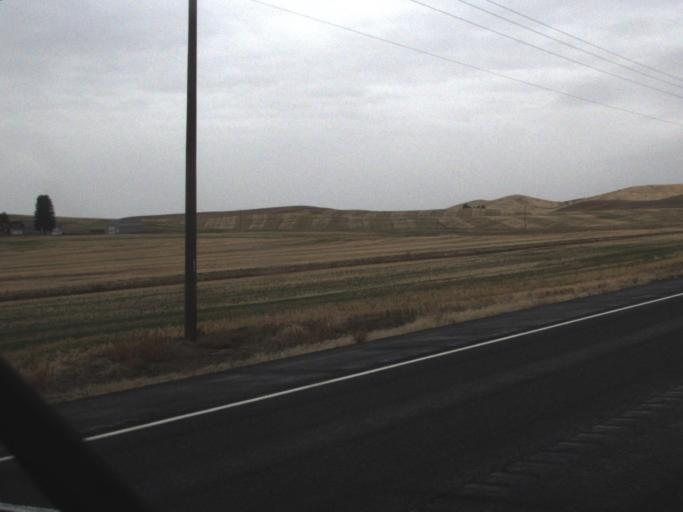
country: US
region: Washington
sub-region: Whitman County
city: Colfax
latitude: 46.7854
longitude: -117.3041
